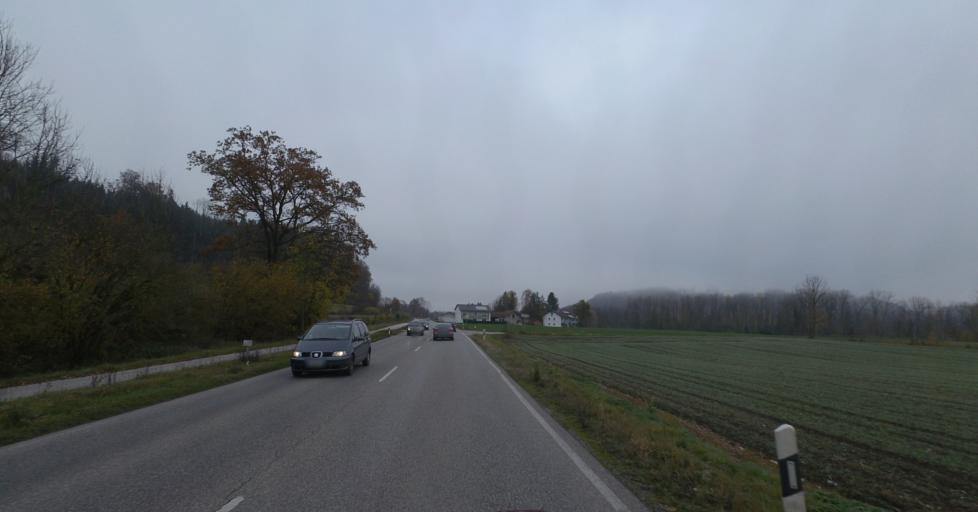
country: DE
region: Bavaria
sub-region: Upper Bavaria
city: Engelsberg
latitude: 48.1108
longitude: 12.5688
